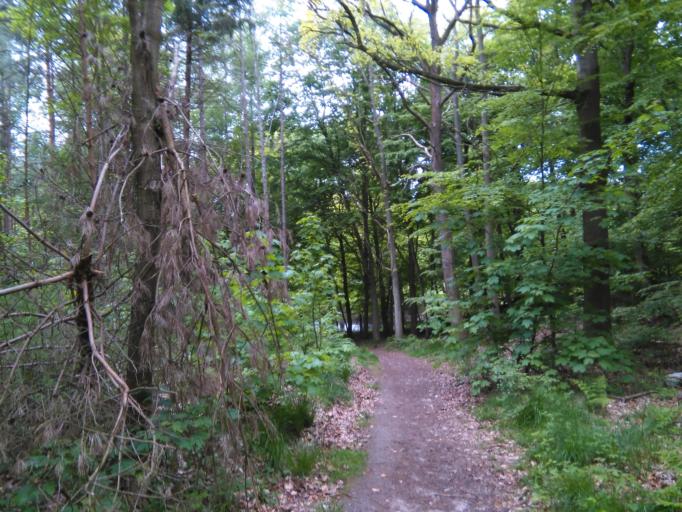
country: DK
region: Central Jutland
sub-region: Arhus Kommune
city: Arhus
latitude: 56.1189
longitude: 10.2210
